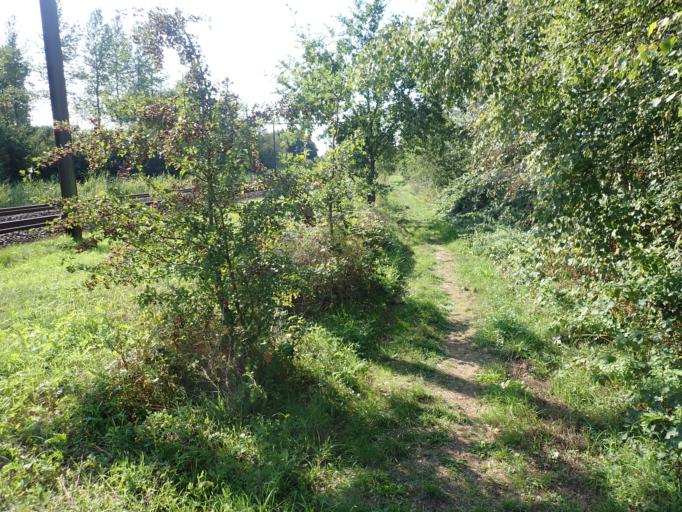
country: BE
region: Flanders
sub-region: Provincie Vlaams-Brabant
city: Scherpenheuvel-Zichem
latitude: 51.0076
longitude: 4.9835
